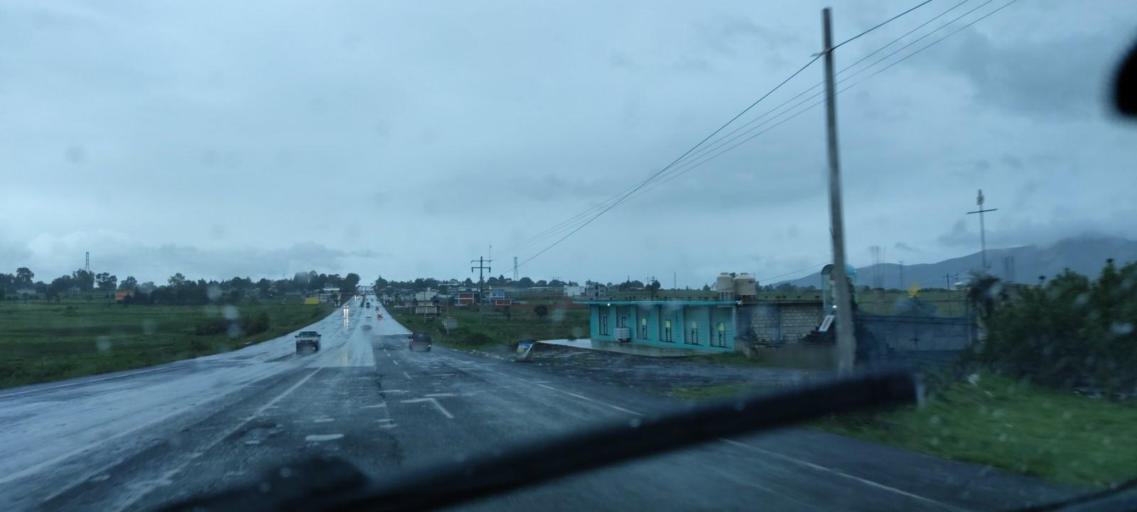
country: MX
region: Mexico
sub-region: Jilotepec
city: Doxhicho
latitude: 19.9190
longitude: -99.5947
